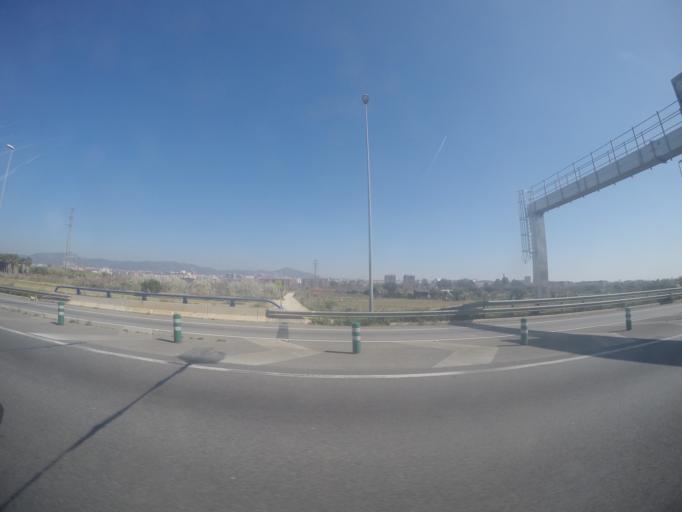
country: ES
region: Catalonia
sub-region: Provincia de Barcelona
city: Sant Joan Despi
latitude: 41.3552
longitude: 2.0533
